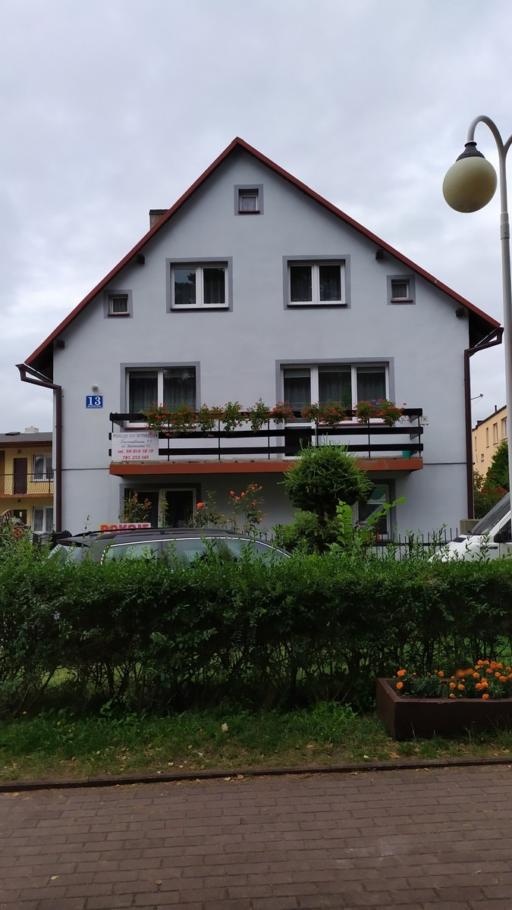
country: PL
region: Pomeranian Voivodeship
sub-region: Powiat slupski
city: Smoldzino
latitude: 54.6646
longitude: 17.0500
